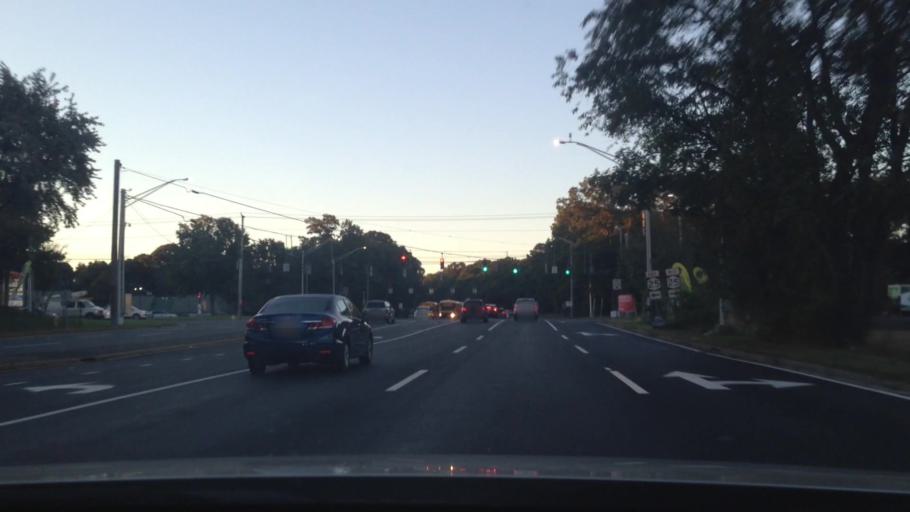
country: US
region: New York
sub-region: Suffolk County
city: Selden
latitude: 40.8687
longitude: -73.0237
